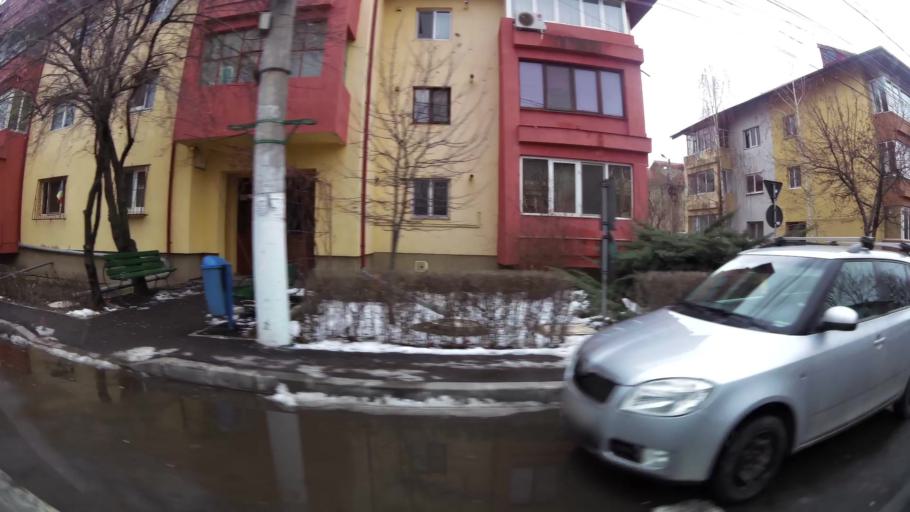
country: RO
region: Ilfov
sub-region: Comuna Otopeni
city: Otopeni
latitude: 44.5537
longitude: 26.0705
